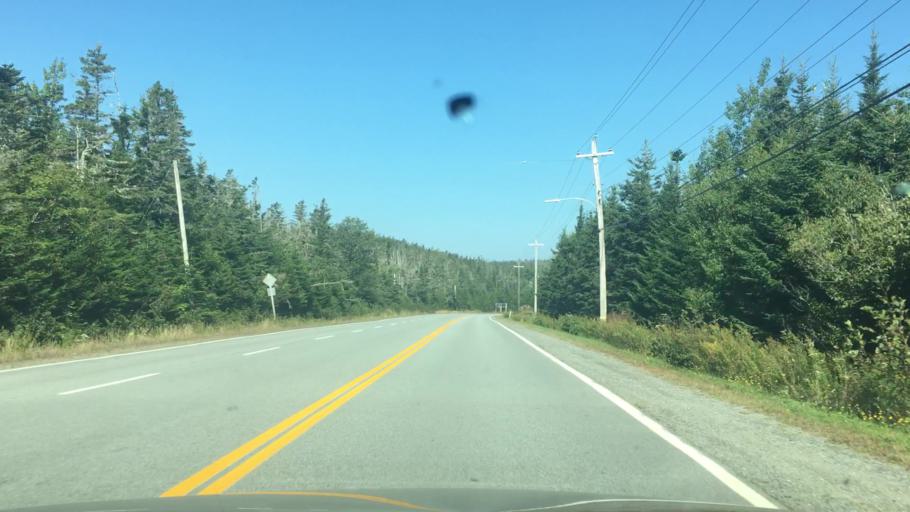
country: CA
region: Nova Scotia
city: New Glasgow
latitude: 44.8167
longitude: -62.6321
